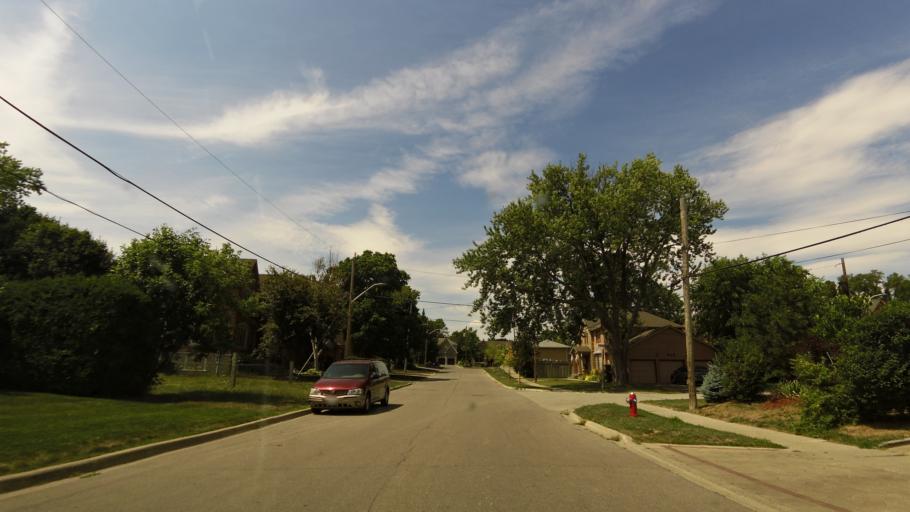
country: CA
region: Ontario
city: Mississauga
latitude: 43.5696
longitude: -79.5791
